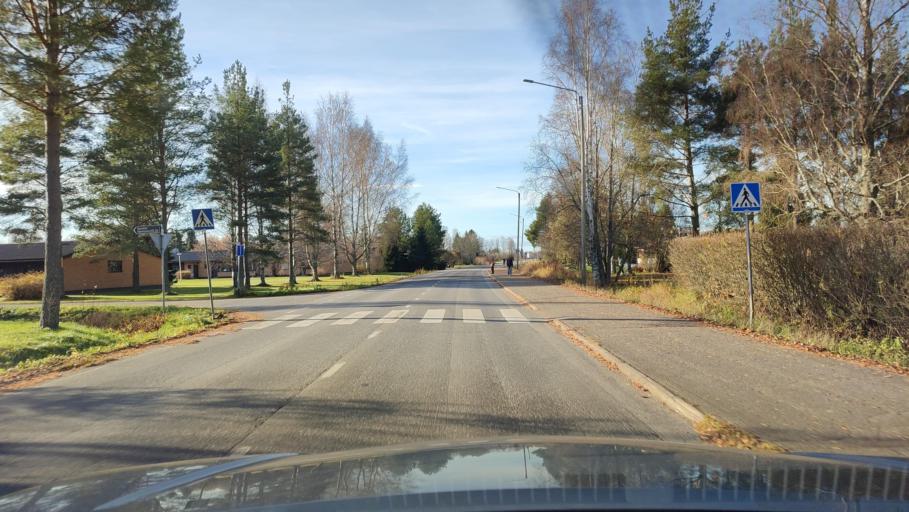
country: FI
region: Southern Ostrobothnia
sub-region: Suupohja
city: Teuva
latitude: 62.4772
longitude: 21.7293
